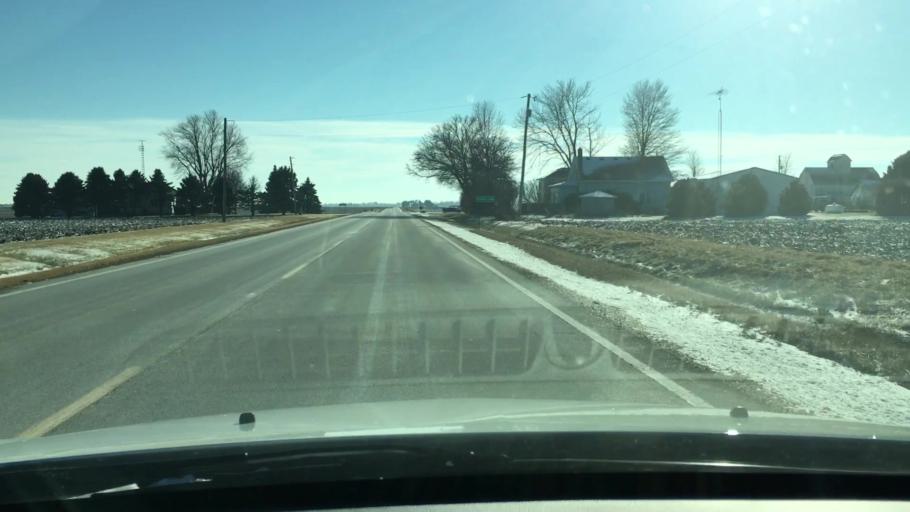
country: US
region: Illinois
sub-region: Ogle County
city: Rochelle
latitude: 41.8843
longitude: -89.0731
